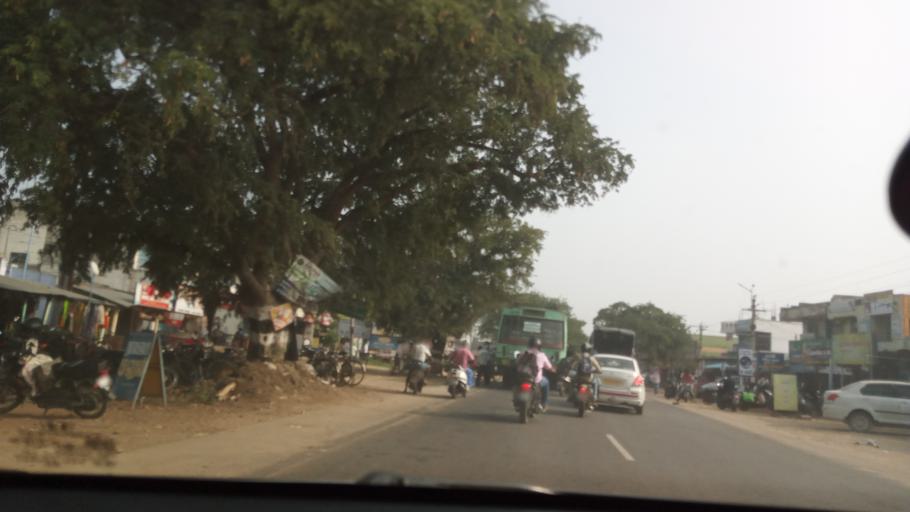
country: IN
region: Tamil Nadu
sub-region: Coimbatore
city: Annur
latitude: 11.1742
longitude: 77.0567
